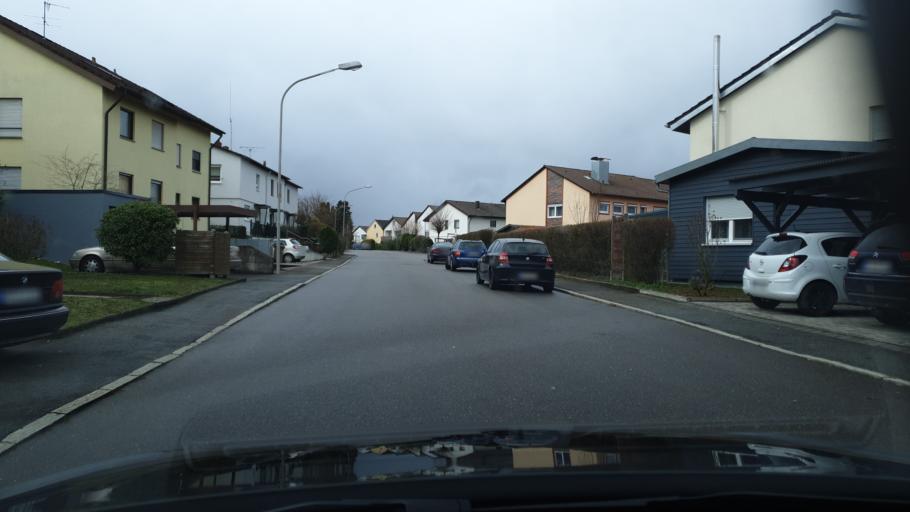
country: DE
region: Baden-Wuerttemberg
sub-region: Regierungsbezirk Stuttgart
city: Leingarten
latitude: 49.1410
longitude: 9.1320
